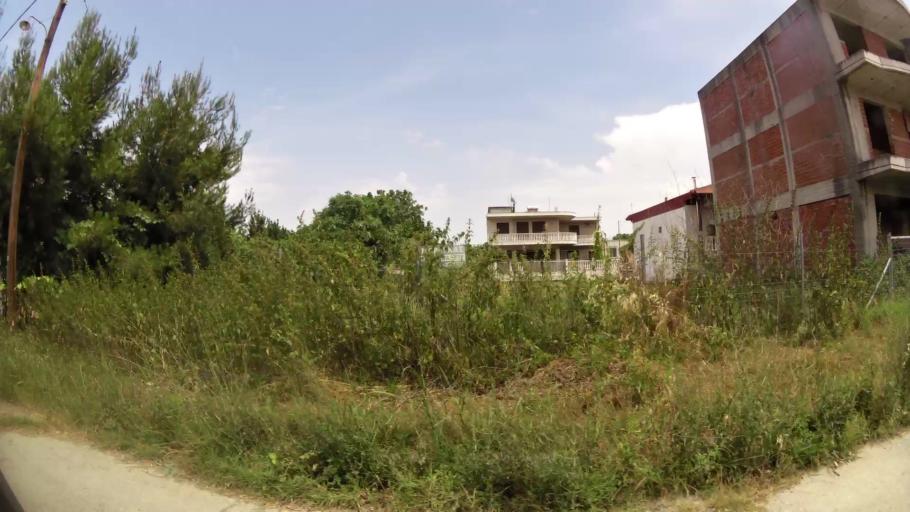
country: GR
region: Central Macedonia
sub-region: Nomos Pierias
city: Peristasi
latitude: 40.2622
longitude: 22.5360
